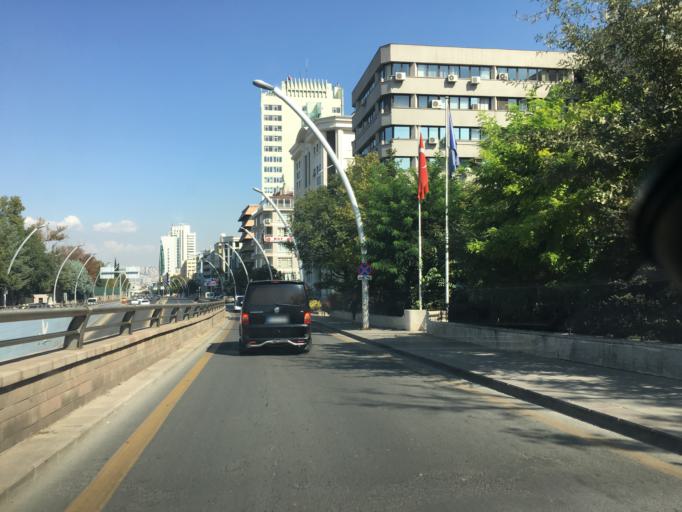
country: TR
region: Ankara
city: Cankaya
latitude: 39.9023
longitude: 32.8593
